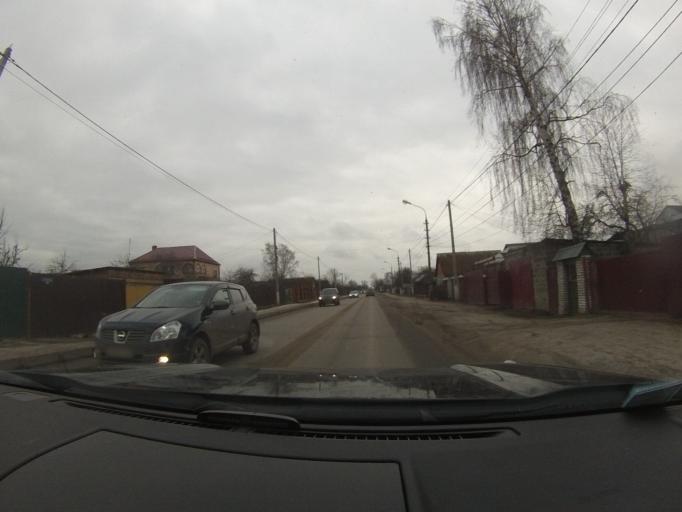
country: RU
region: Moskovskaya
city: Lopatinskiy
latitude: 55.3295
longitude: 38.7119
